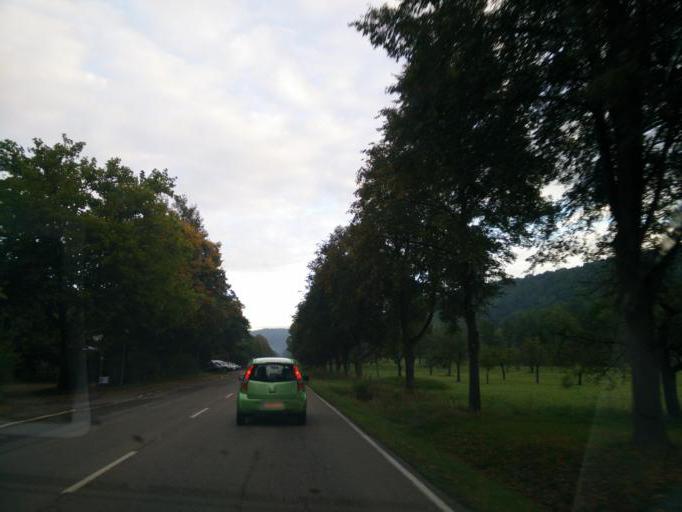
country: DE
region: Baden-Wuerttemberg
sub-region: Tuebingen Region
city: Tuebingen
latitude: 48.5338
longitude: 9.0774
